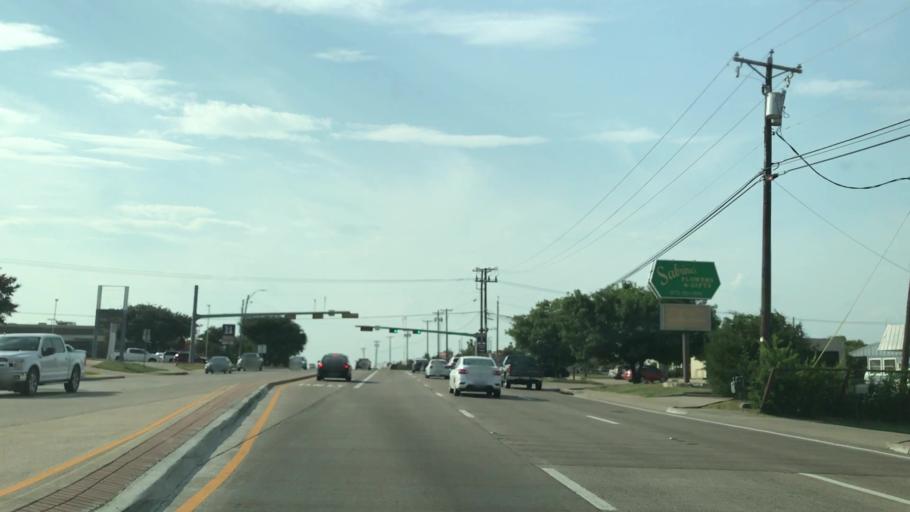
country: US
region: Texas
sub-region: Rockwall County
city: Rockwall
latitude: 32.9118
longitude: -96.4518
